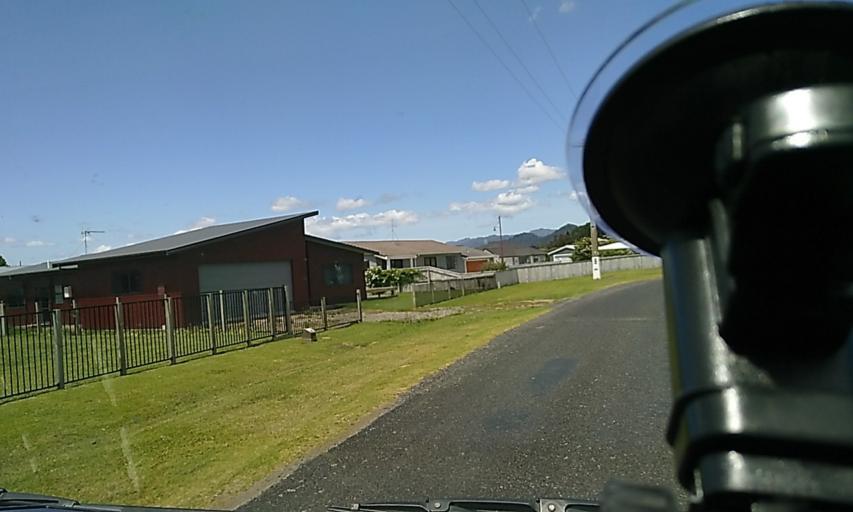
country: NZ
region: Bay of Plenty
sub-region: Western Bay of Plenty District
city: Waihi Beach
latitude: -37.4463
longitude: 175.9605
